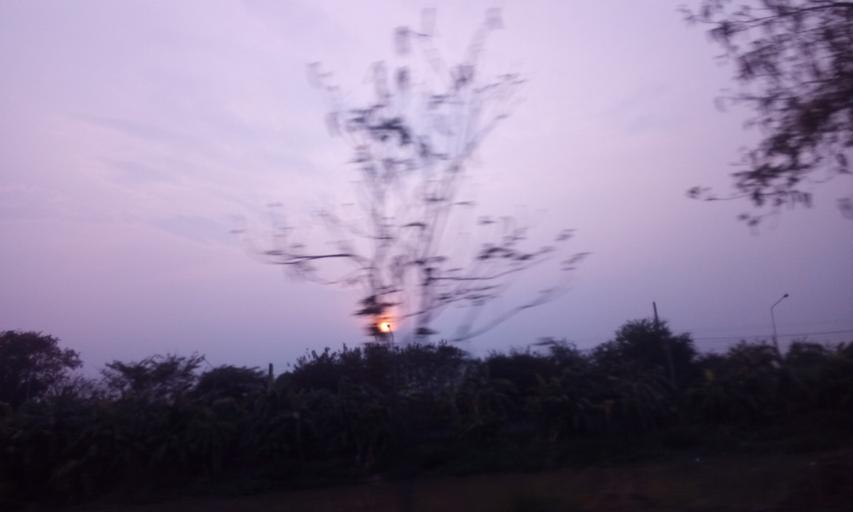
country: TH
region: Bangkok
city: Nong Chok
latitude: 13.9675
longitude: 100.8956
